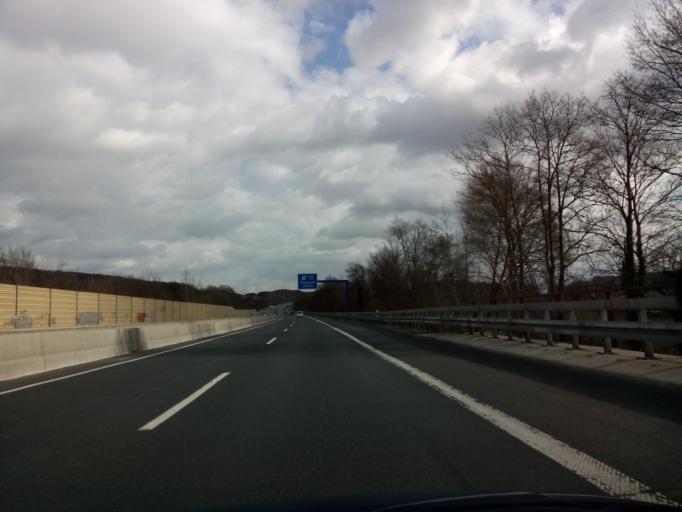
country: DE
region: Lower Saxony
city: Bissendorf
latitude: 52.2428
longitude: 8.1135
